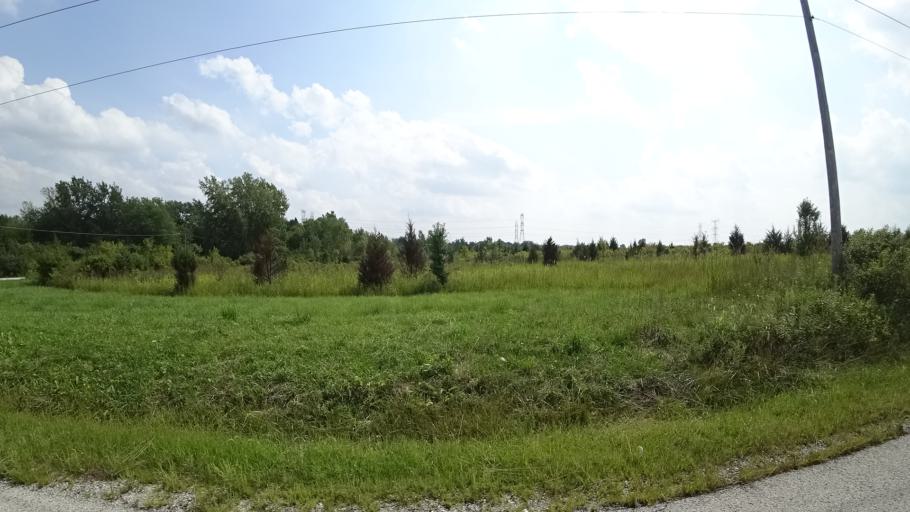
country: US
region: Illinois
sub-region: Cook County
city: Orland Park
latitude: 41.6443
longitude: -87.8887
